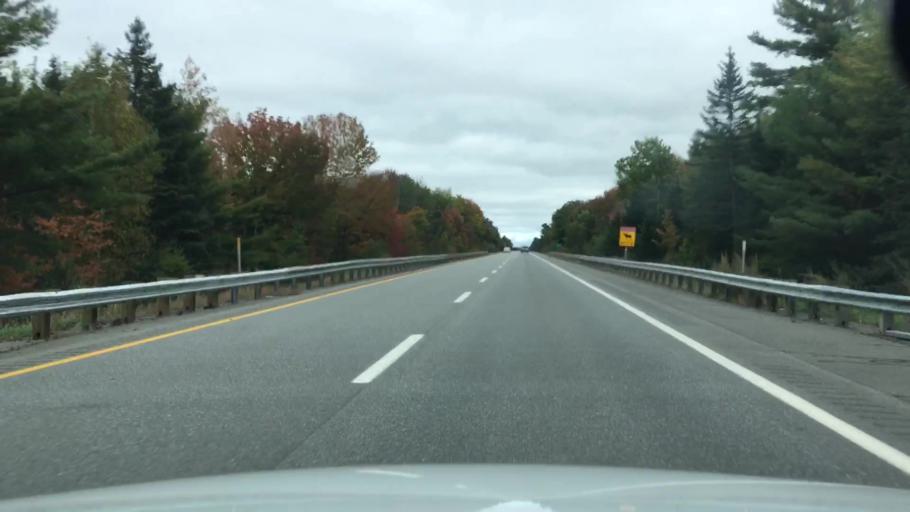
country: US
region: Maine
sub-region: Penobscot County
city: Plymouth
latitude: 44.7893
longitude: -69.1823
